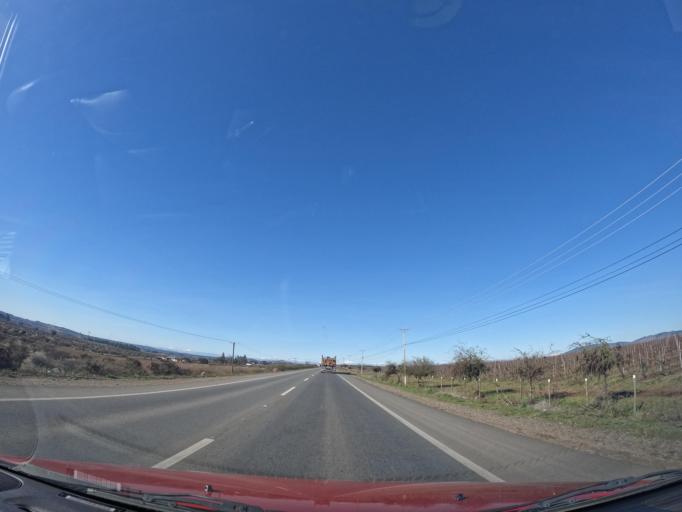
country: CL
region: Maule
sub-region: Provincia de Cauquenes
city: Cauquenes
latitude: -35.9634
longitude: -72.2403
